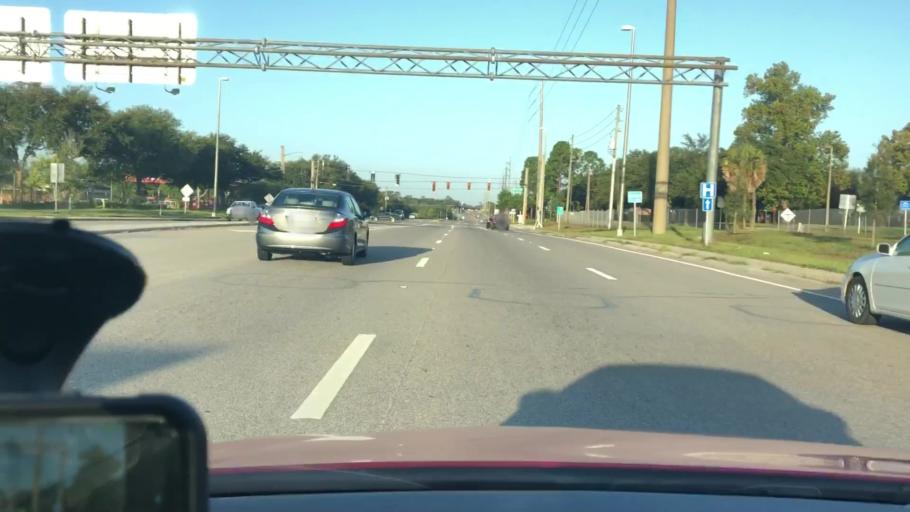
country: US
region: Florida
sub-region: Volusia County
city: Deltona
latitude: 28.9112
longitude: -81.2746
